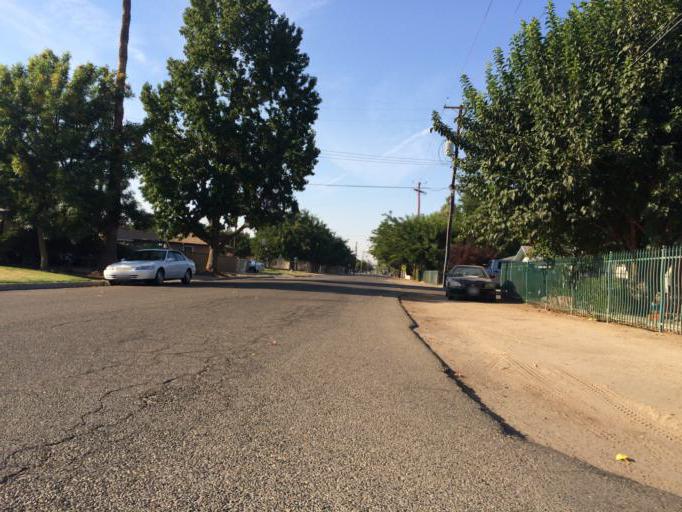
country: US
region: California
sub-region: Fresno County
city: Sunnyside
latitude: 36.7478
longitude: -119.7319
